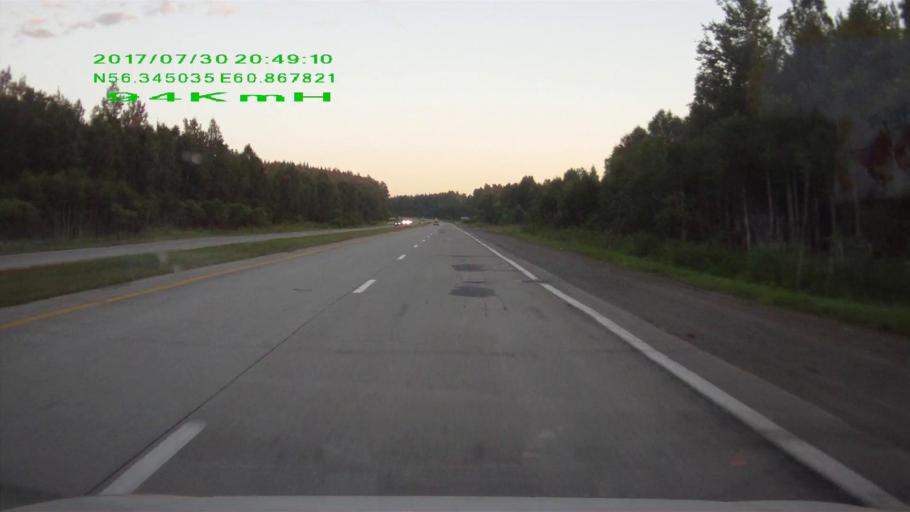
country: RU
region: Sverdlovsk
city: Shchelkun
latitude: 56.3445
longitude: 60.8677
